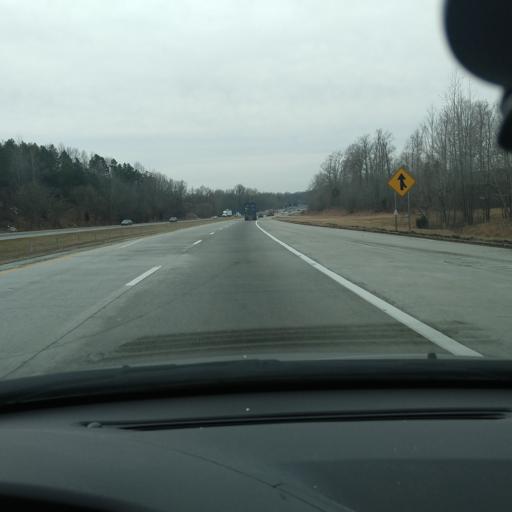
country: US
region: North Carolina
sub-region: Davidson County
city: Lexington
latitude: 35.7986
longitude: -80.2938
